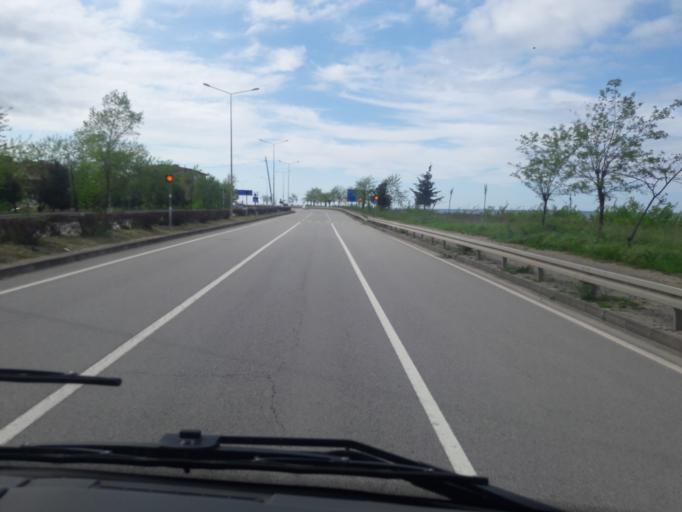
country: TR
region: Giresun
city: Piraziz
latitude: 40.9557
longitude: 38.1198
